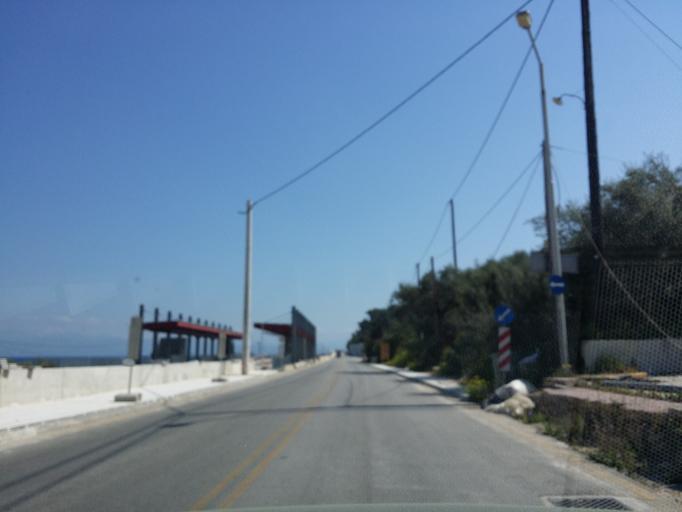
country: GR
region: West Greece
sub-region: Nomos Achaias
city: Akrata
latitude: 38.1703
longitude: 22.2776
